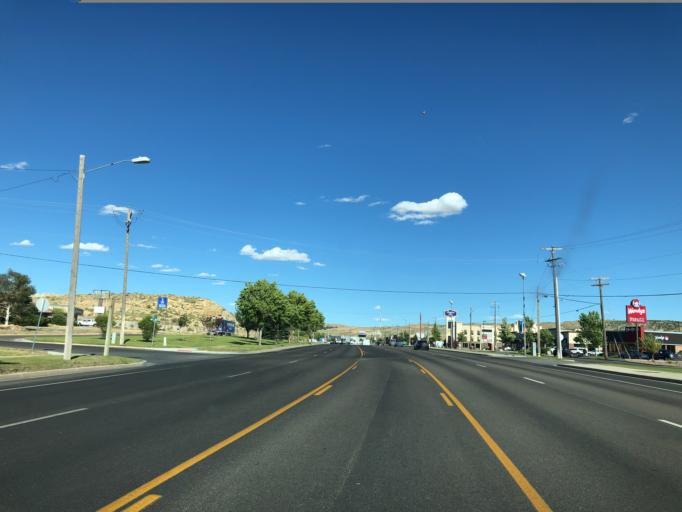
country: US
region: Wyoming
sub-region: Sweetwater County
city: Rock Springs
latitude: 41.5752
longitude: -109.2482
